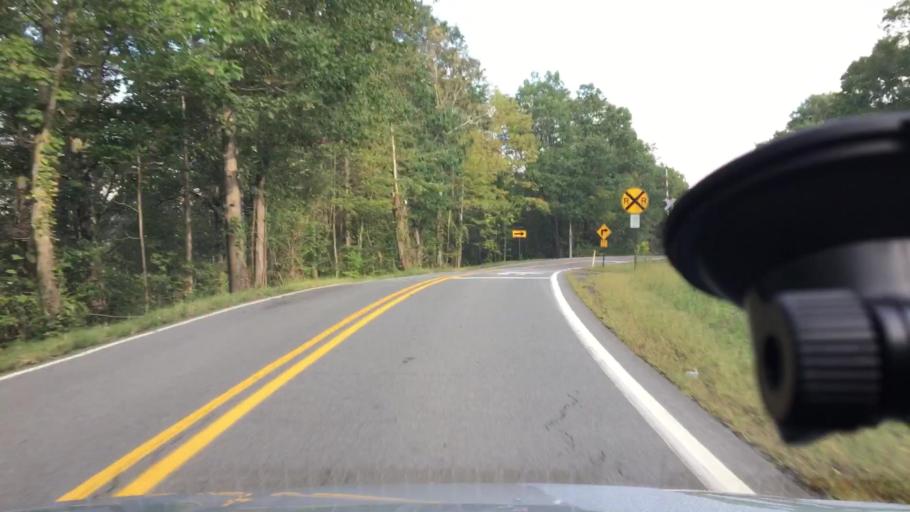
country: US
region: Pennsylvania
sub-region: Monroe County
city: Parkside
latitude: 41.1310
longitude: -75.2639
